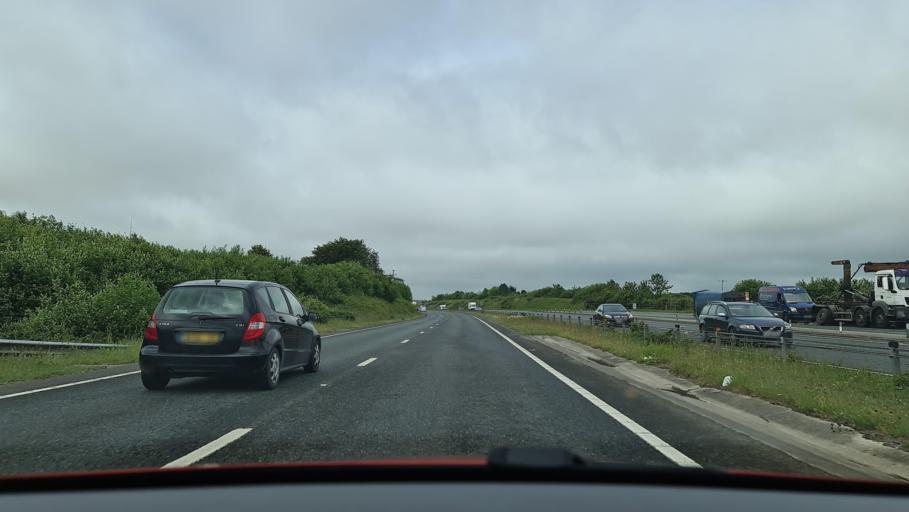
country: GB
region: England
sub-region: Cornwall
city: Bugle
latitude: 50.4297
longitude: -4.8014
